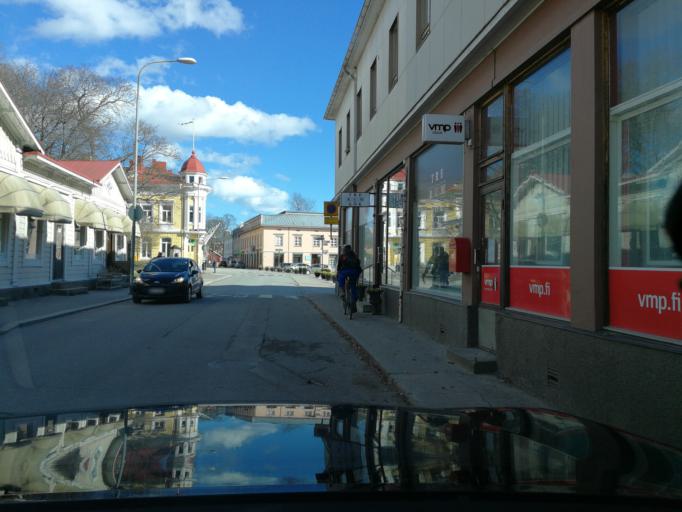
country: FI
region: Uusimaa
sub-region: Raaseporin
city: Ekenaes
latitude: 59.9749
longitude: 23.4346
